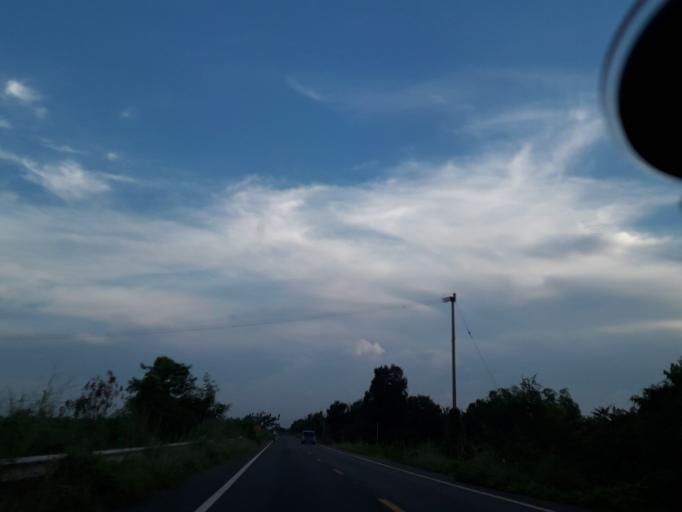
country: TH
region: Sara Buri
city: Nong Khae
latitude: 14.2933
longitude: 100.8911
